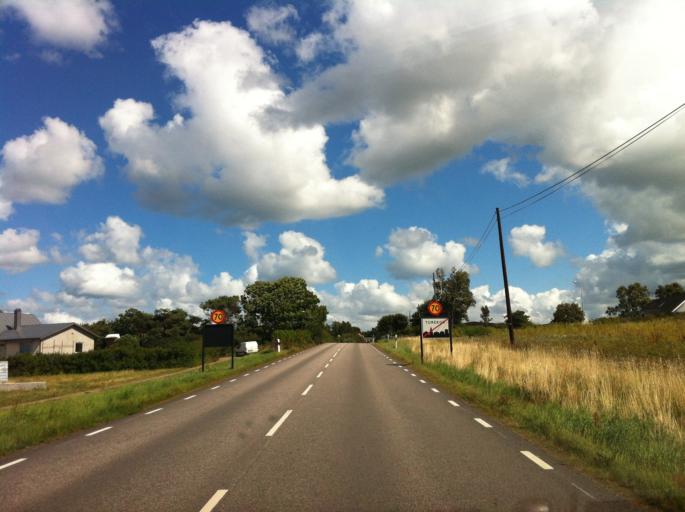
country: SE
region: Skane
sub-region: Bastads Kommun
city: Forslov
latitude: 56.2970
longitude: 12.8295
